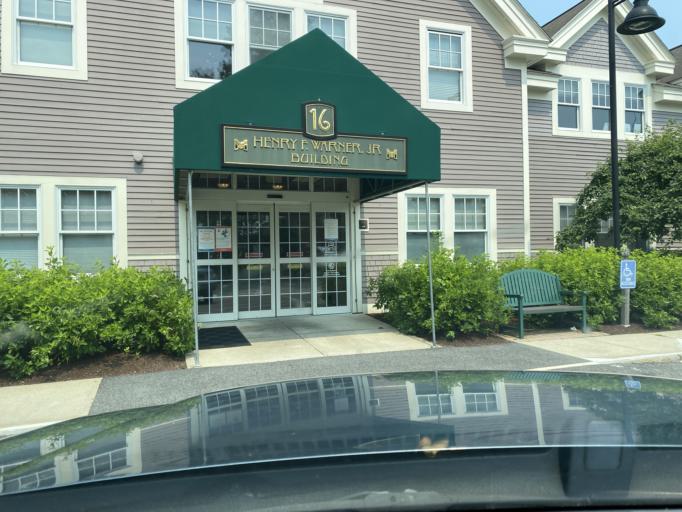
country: US
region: Maine
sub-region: York County
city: York Harbor
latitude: 43.1428
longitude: -70.6510
